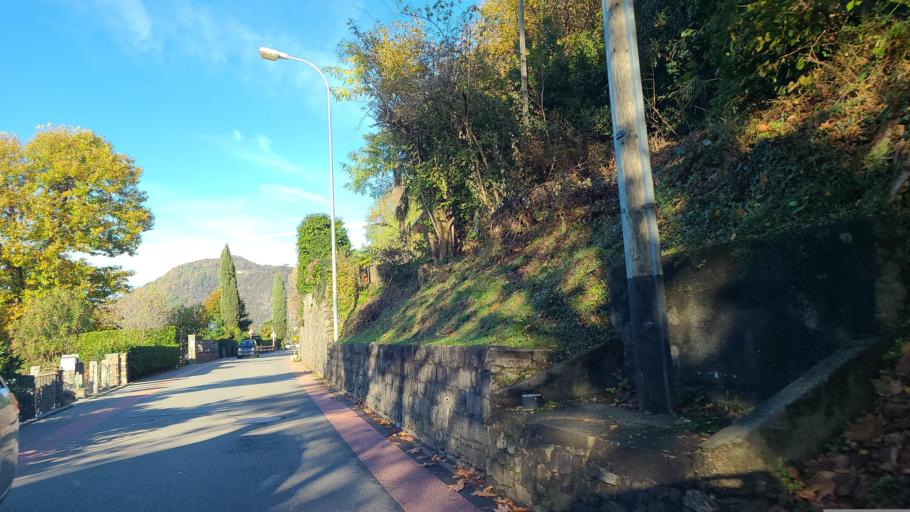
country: IT
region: Lombardy
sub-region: Provincia di Varese
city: Brusimpiano
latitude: 45.9395
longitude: 8.9005
